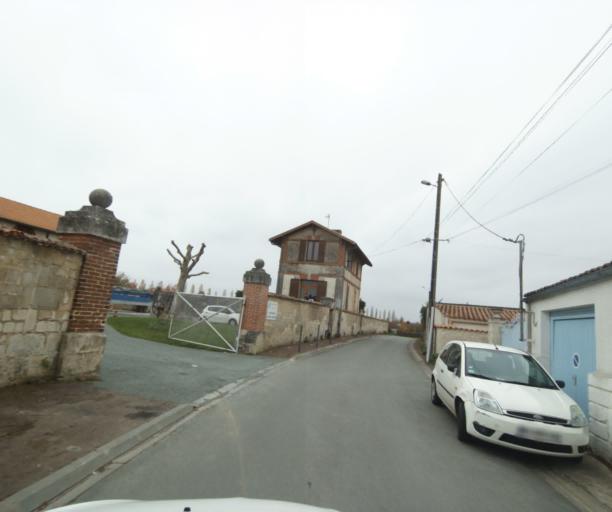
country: FR
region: Poitou-Charentes
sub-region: Departement de la Charente-Maritime
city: Les Gonds
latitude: 45.7290
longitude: -0.6190
